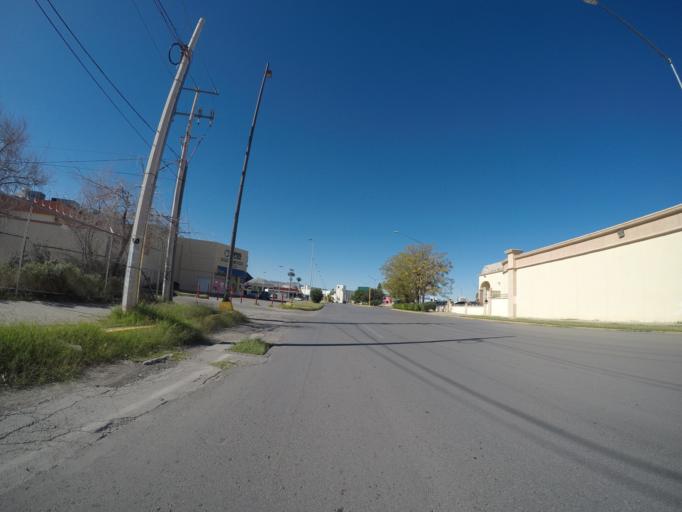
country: MX
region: Chihuahua
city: Ciudad Juarez
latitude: 31.7426
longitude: -106.4514
